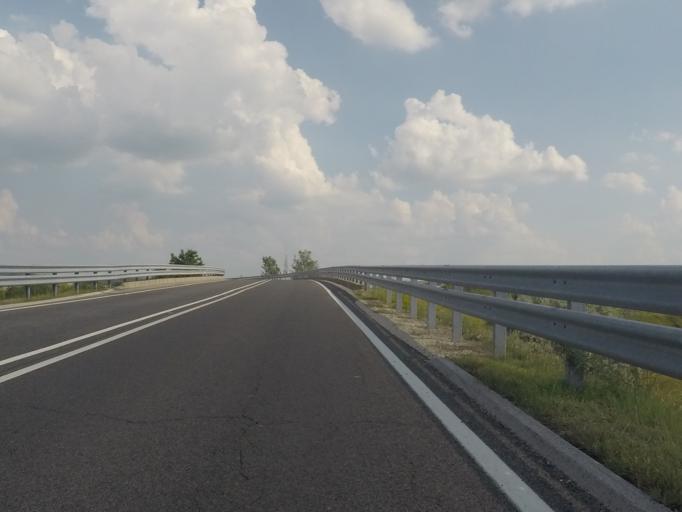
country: HU
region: Somogy
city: Zamardi
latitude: 46.8802
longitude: 17.9734
